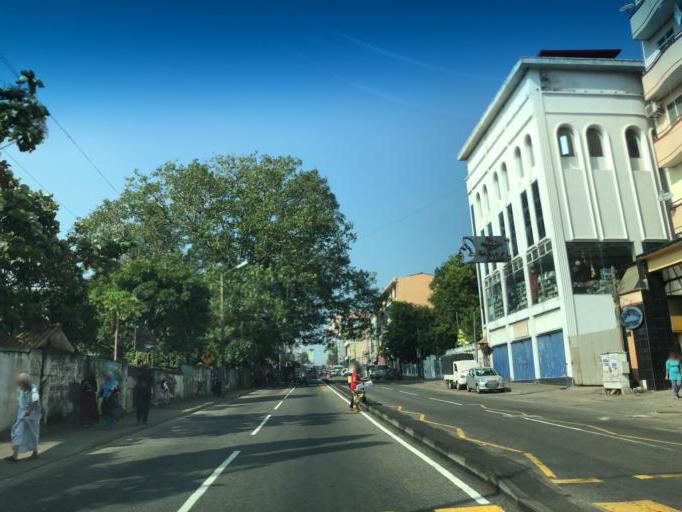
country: LK
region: Western
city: Colombo
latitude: 6.9430
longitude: 79.8635
